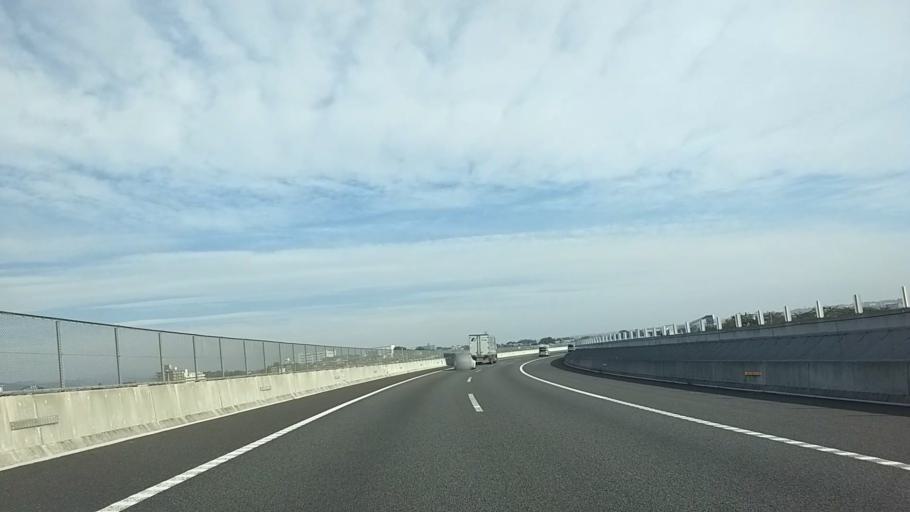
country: JP
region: Kanagawa
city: Atsugi
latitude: 35.4570
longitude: 139.3722
